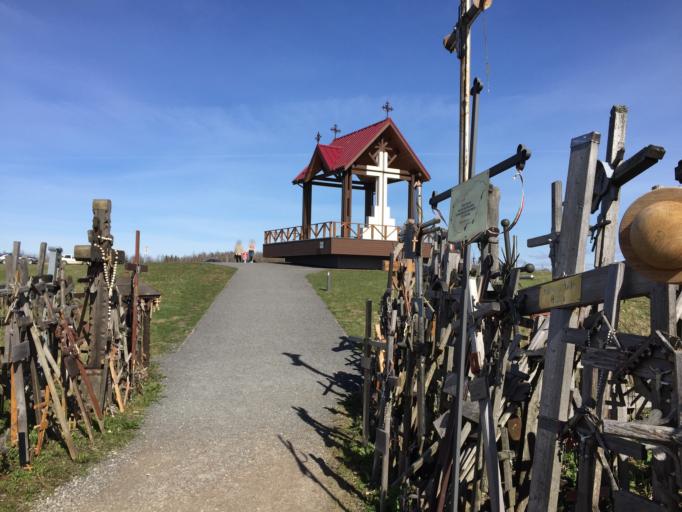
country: LT
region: Siauliu apskritis
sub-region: Siauliai
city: Siauliai
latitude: 56.0155
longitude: 23.4156
